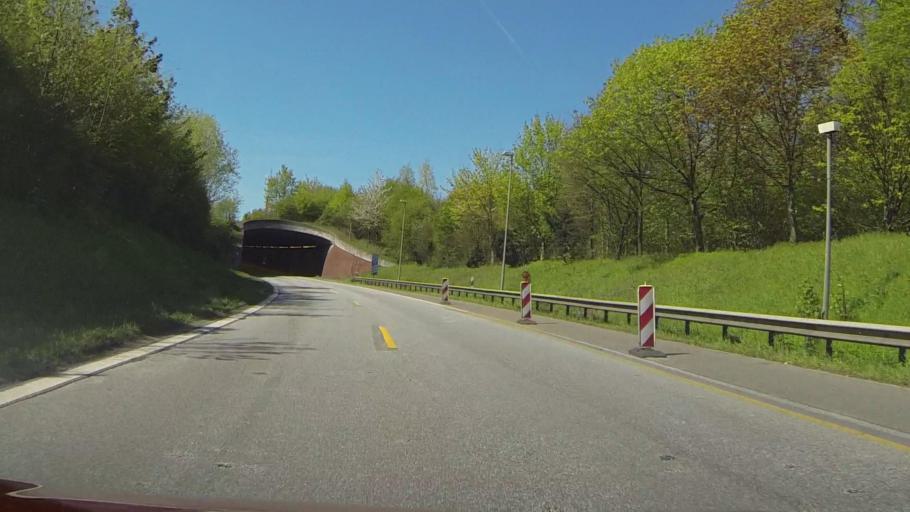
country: DE
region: Hamburg
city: Eidelstedt
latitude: 53.6139
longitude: 9.9151
